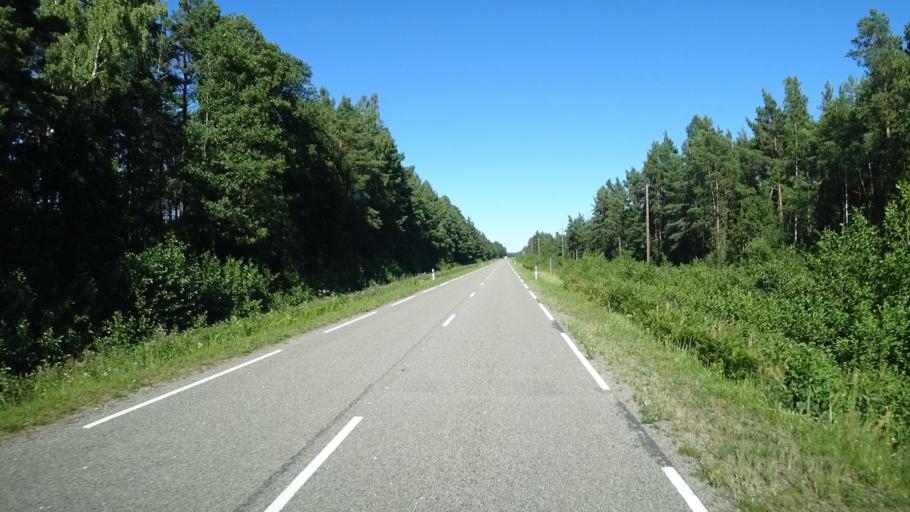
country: LV
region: Dundaga
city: Dundaga
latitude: 57.7064
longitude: 22.4358
